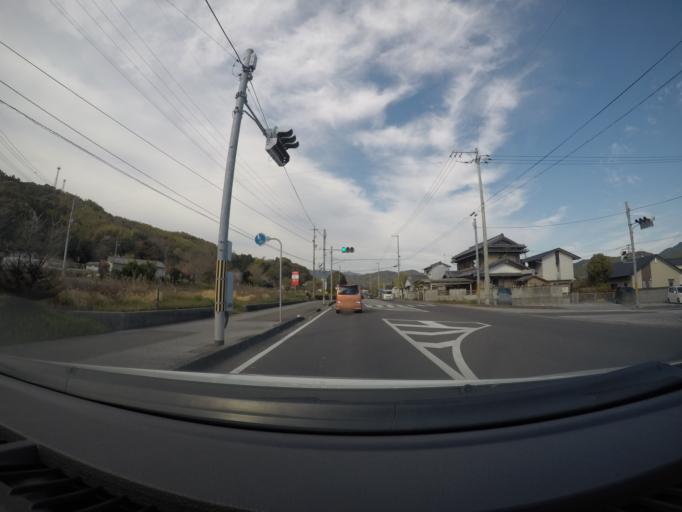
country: JP
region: Kochi
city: Kochi-shi
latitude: 33.6133
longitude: 133.7113
